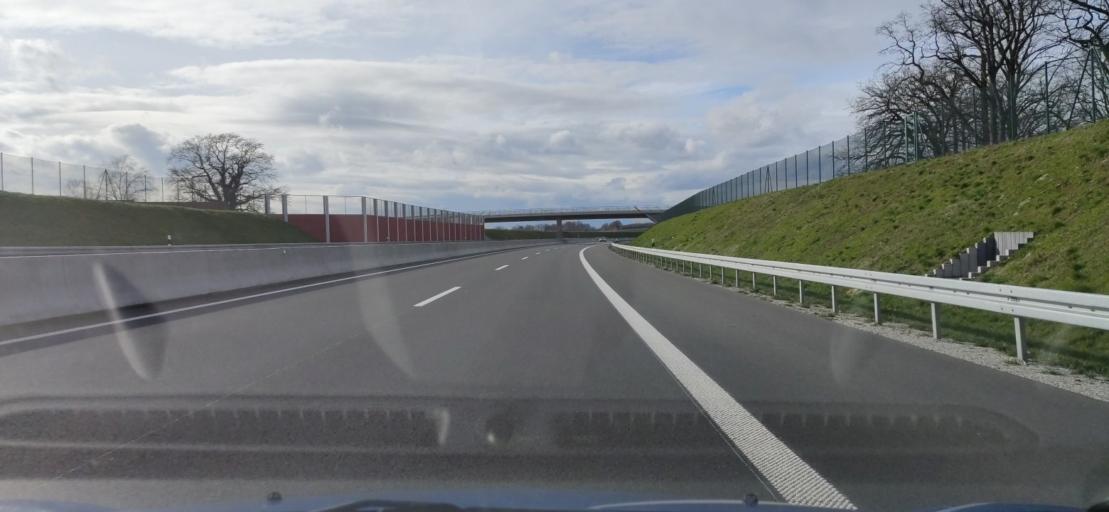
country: DE
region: North Rhine-Westphalia
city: Borgholzhausen
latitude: 52.0676
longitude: 8.2715
